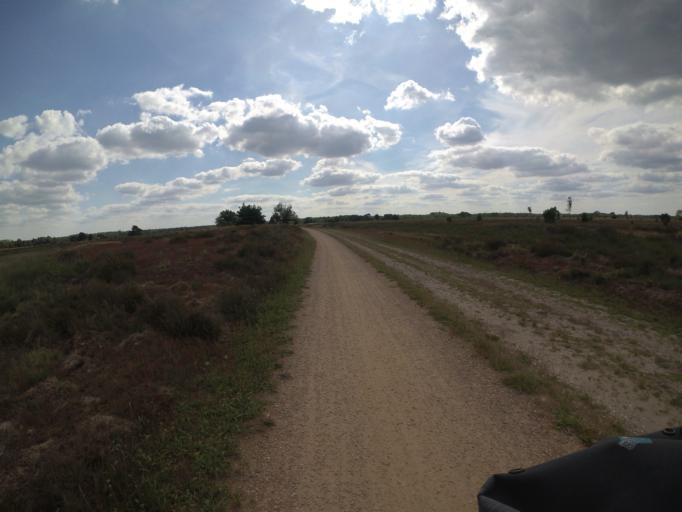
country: NL
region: North Brabant
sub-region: Gemeente Heeze-Leende
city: Heeze
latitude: 51.3981
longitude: 5.6085
